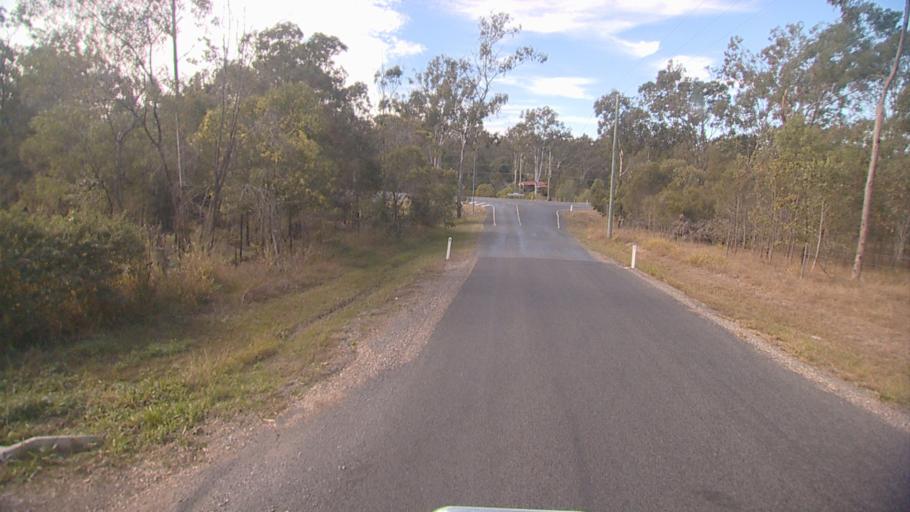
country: AU
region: Queensland
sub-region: Logan
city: North Maclean
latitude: -27.7740
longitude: 152.9798
